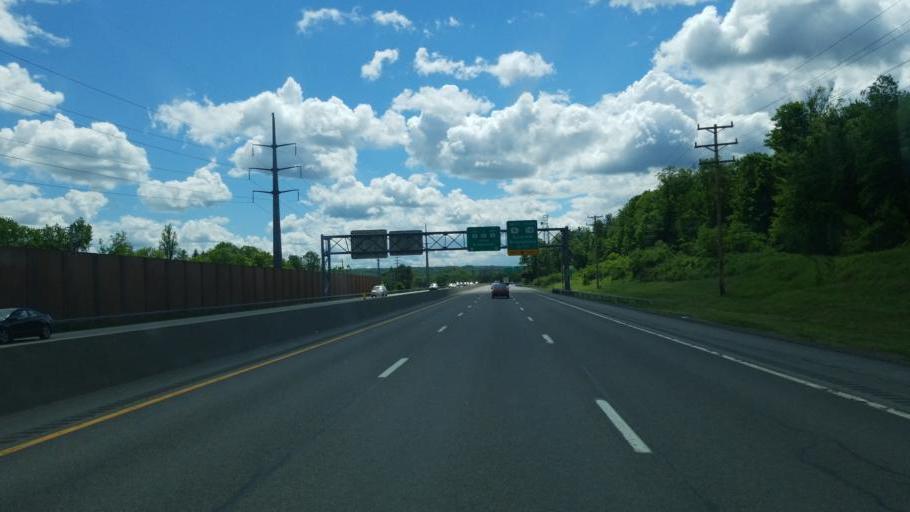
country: US
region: New York
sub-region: Oneida County
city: New Hartford
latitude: 43.0872
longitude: -75.3015
